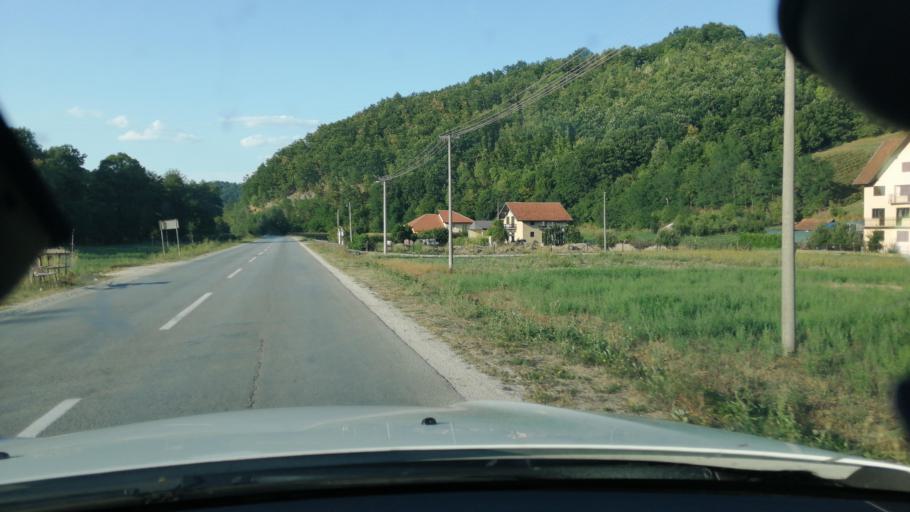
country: RS
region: Central Serbia
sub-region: Zlatiborski Okrug
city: Arilje
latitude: 43.7430
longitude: 20.2537
